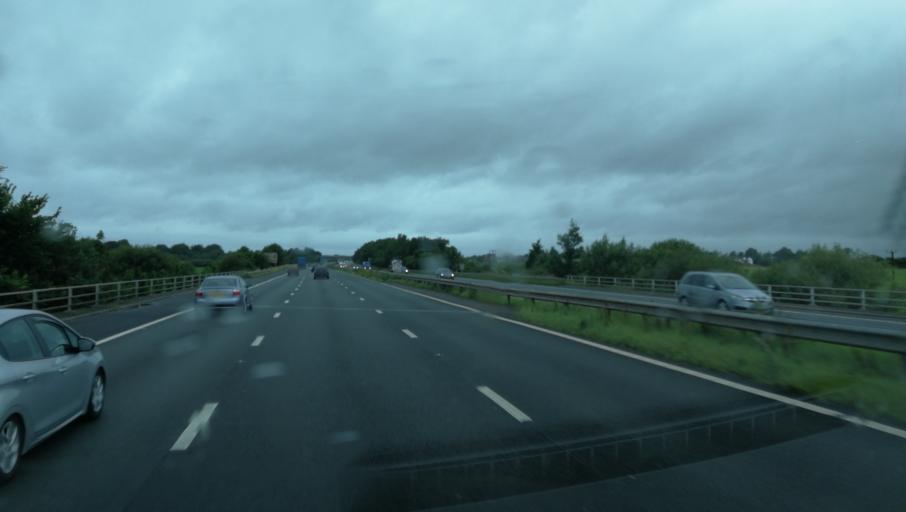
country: GB
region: England
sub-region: Borough of Bolton
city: Westhoughton
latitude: 53.5630
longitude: -2.5147
